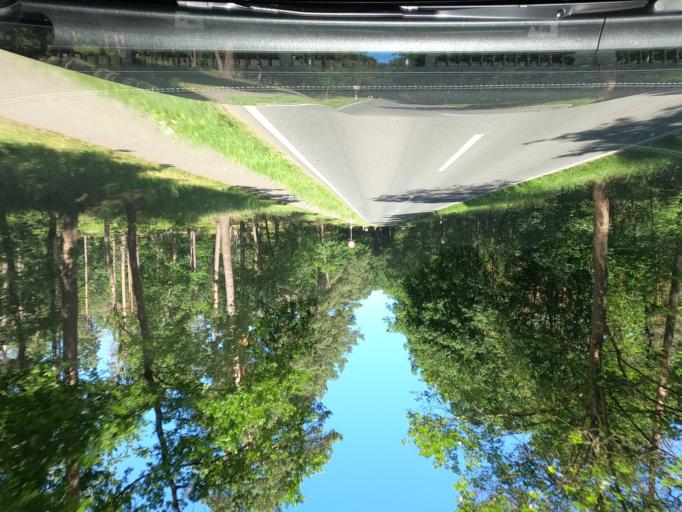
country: DE
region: Lower Saxony
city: Wienhausen
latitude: 52.5702
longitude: 10.1886
